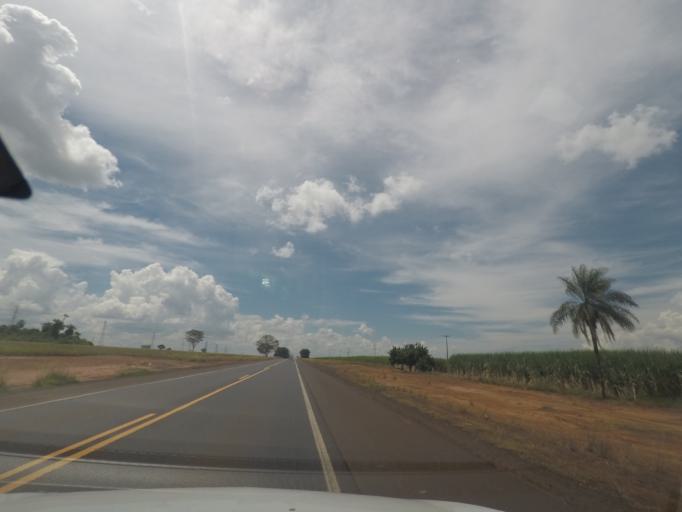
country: BR
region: Sao Paulo
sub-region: Barretos
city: Barretos
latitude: -20.2814
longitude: -48.6712
